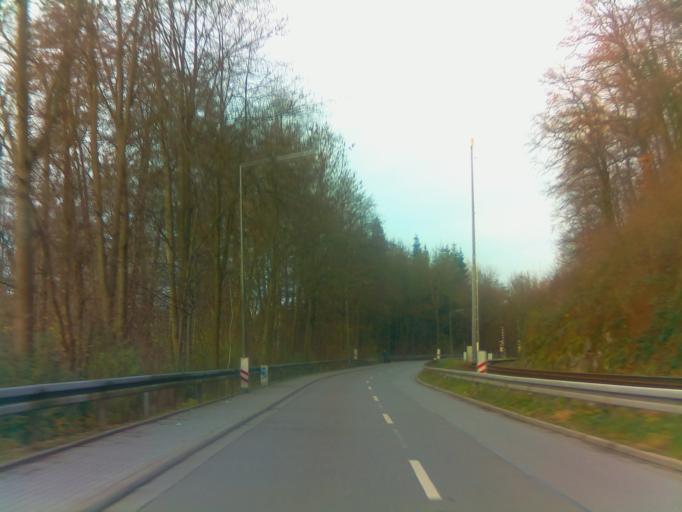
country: DE
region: Hesse
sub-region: Regierungsbezirk Darmstadt
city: Birkenau
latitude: 49.5686
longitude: 8.7121
